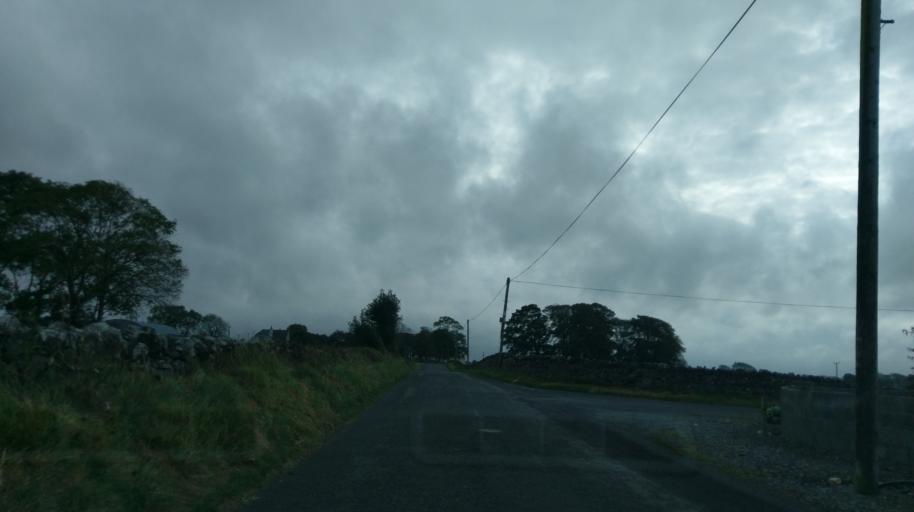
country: IE
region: Connaught
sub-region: County Galway
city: Athenry
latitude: 53.4546
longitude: -8.5884
